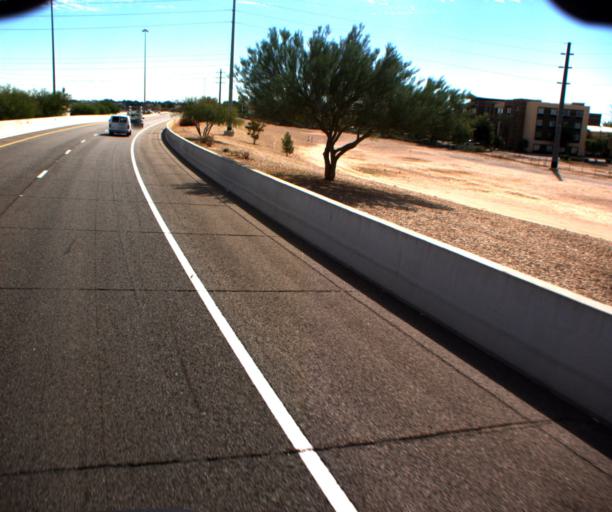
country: US
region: Arizona
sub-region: Maricopa County
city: Chandler
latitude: 33.2904
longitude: -111.8874
